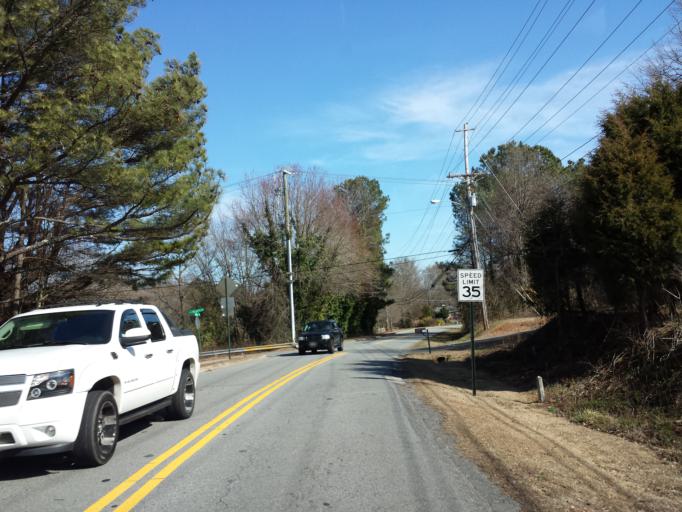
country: US
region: Georgia
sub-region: Cobb County
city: Kennesaw
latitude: 34.0318
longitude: -84.6065
